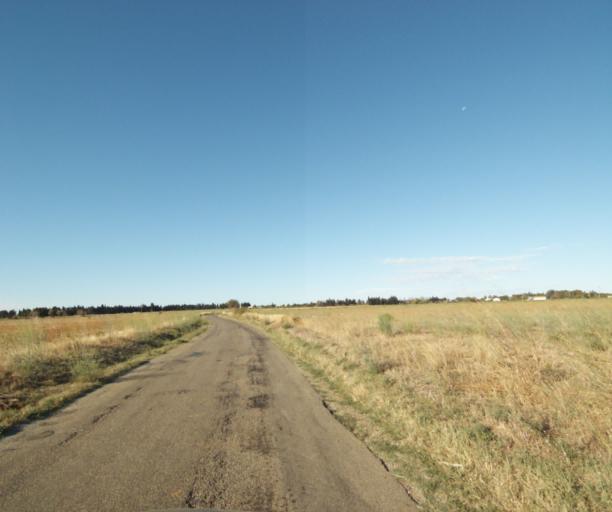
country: FR
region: Languedoc-Roussillon
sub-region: Departement du Gard
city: Bouillargues
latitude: 43.7992
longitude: 4.4462
